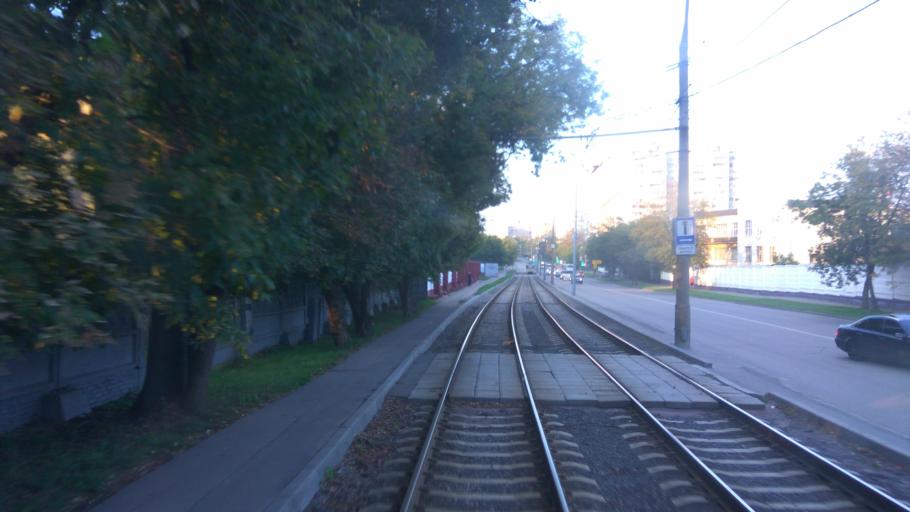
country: RU
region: Moskovskaya
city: Bogorodskoye
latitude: 55.8190
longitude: 37.7465
